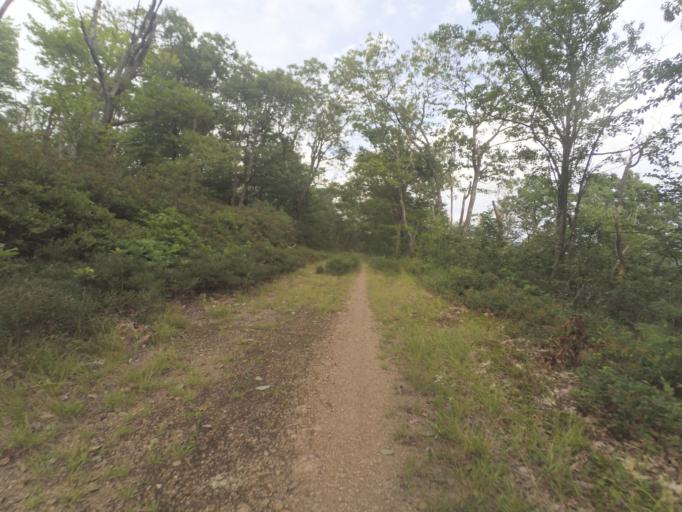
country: US
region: Pennsylvania
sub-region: Centre County
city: Boalsburg
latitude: 40.7175
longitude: -77.7798
